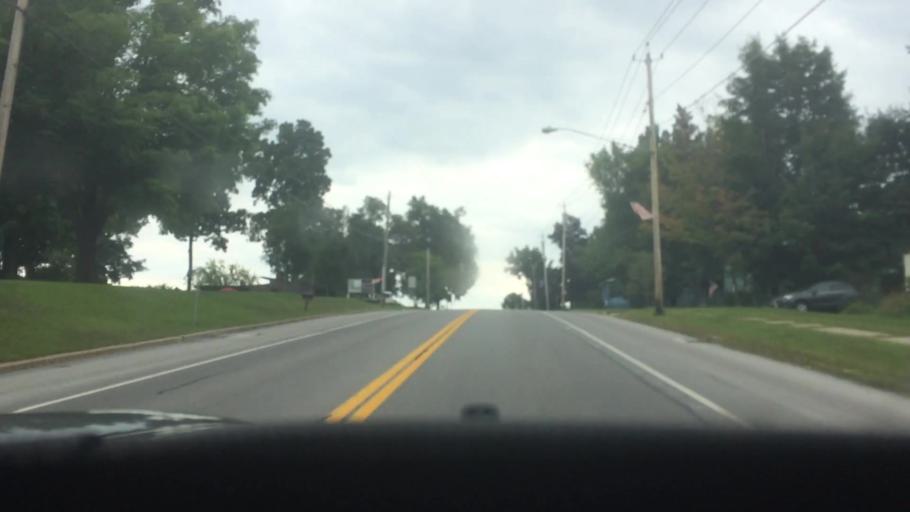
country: US
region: New York
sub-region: St. Lawrence County
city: Ogdensburg
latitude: 44.6143
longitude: -75.4019
